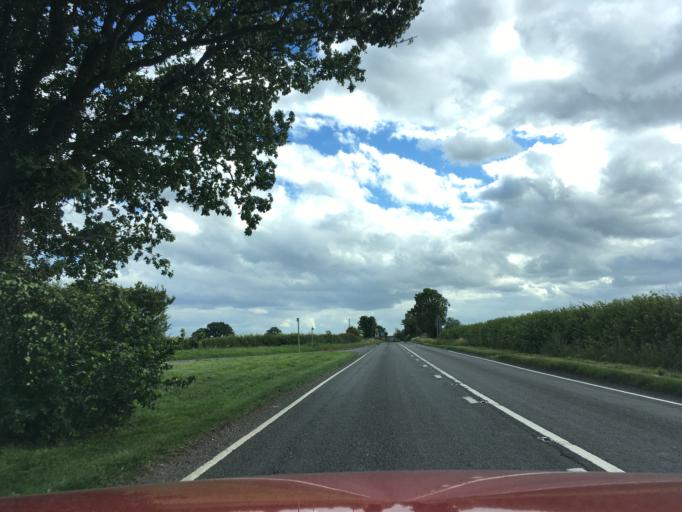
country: GB
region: England
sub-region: Warwickshire
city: Hartshill
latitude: 52.5737
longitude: -1.4791
